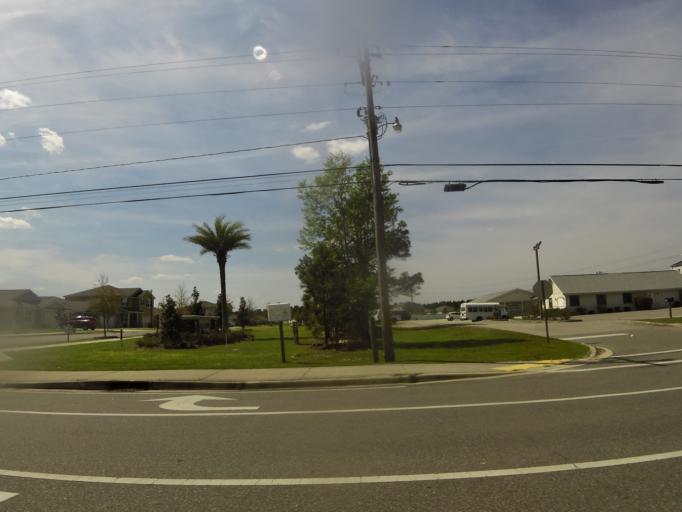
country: US
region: Florida
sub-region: Clay County
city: Middleburg
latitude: 30.0981
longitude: -81.8645
